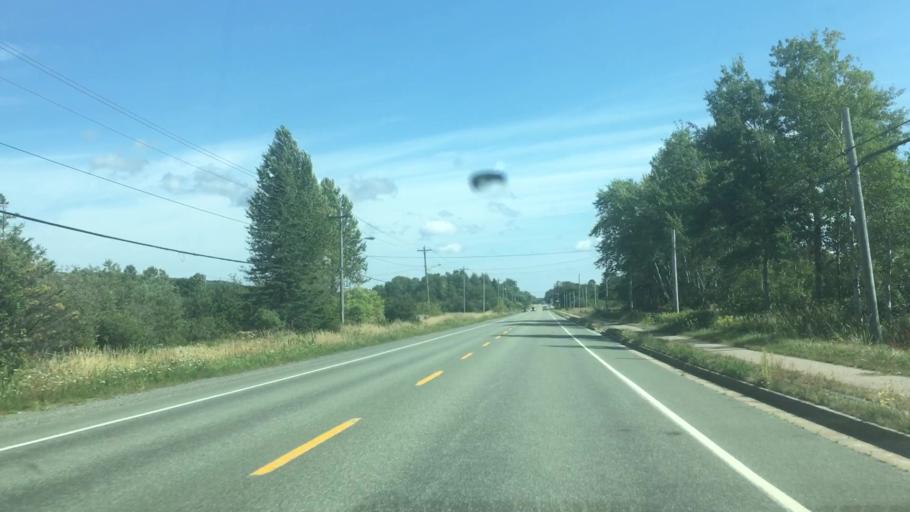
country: CA
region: Nova Scotia
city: Sydney
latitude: 46.0560
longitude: -60.3118
